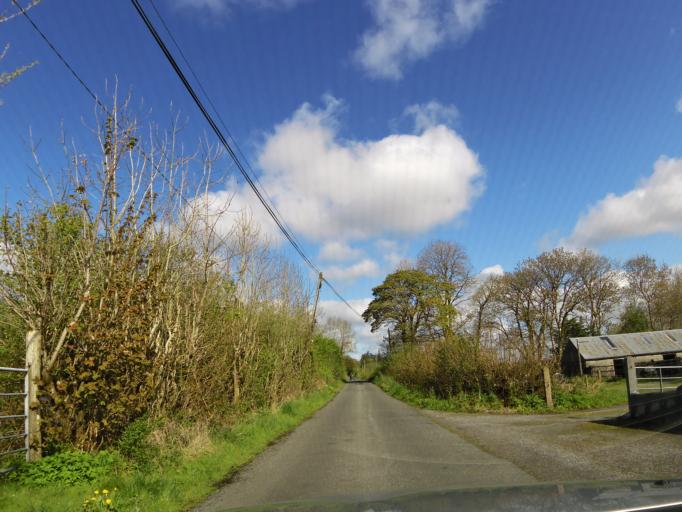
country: IE
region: Connaught
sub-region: Maigh Eo
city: Kiltamagh
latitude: 53.7970
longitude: -8.9666
